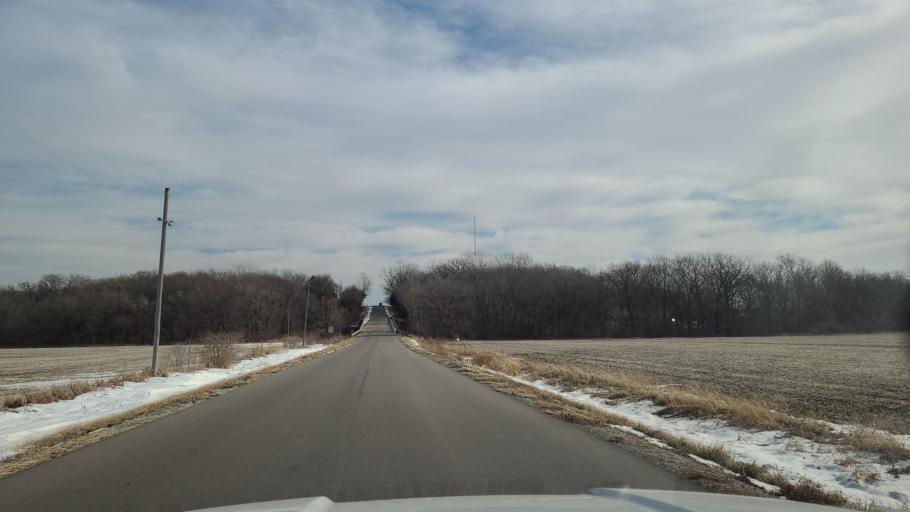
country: US
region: Kansas
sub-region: Douglas County
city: Lawrence
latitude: 38.8990
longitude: -95.1988
